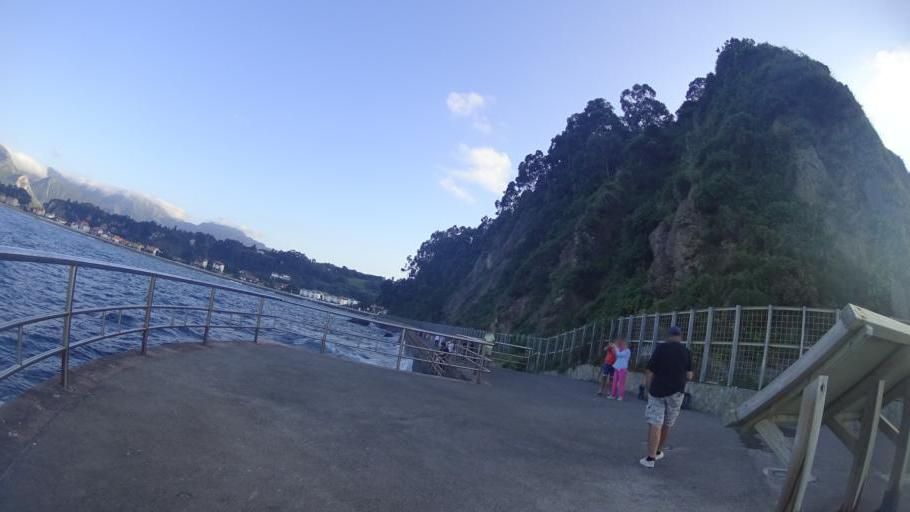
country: ES
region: Asturias
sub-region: Province of Asturias
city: Ribadesella
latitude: 43.4703
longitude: -5.0747
